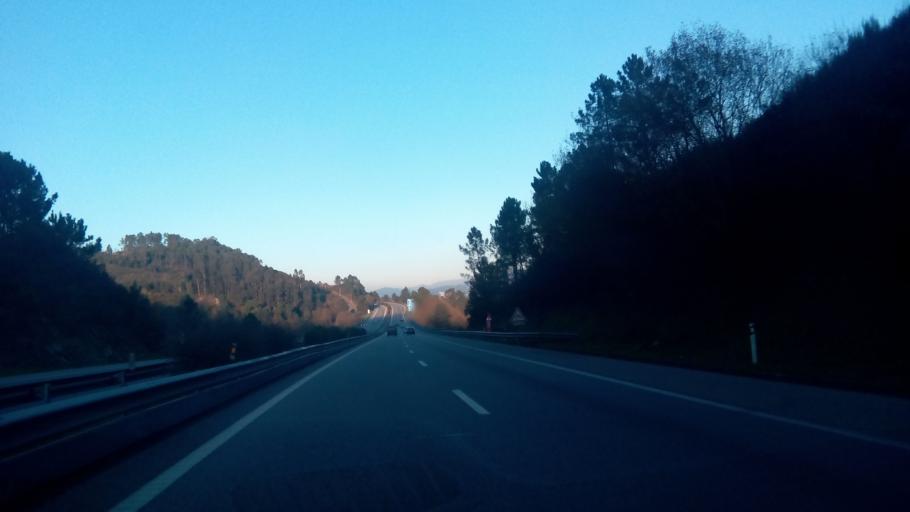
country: PT
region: Porto
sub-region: Amarante
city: Amarante
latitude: 41.2412
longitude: -8.1177
